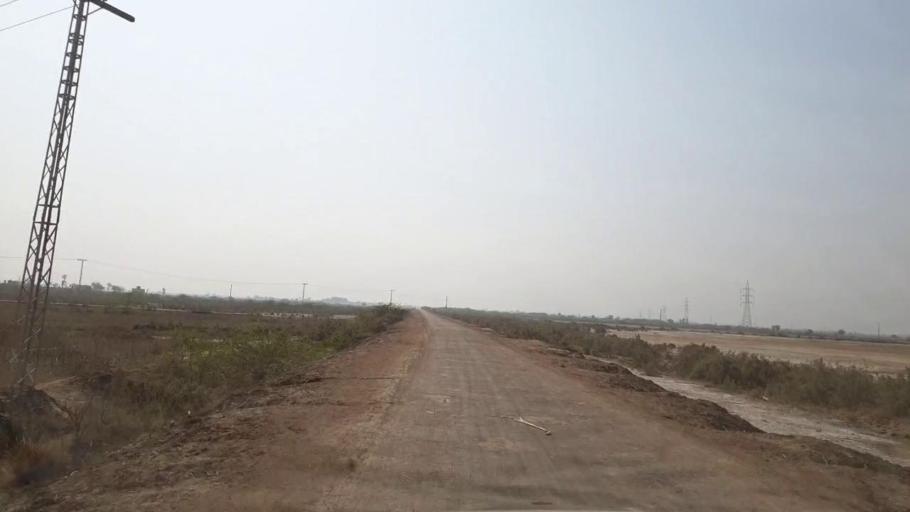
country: PK
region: Sindh
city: Mirpur Khas
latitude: 25.5892
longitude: 69.0253
